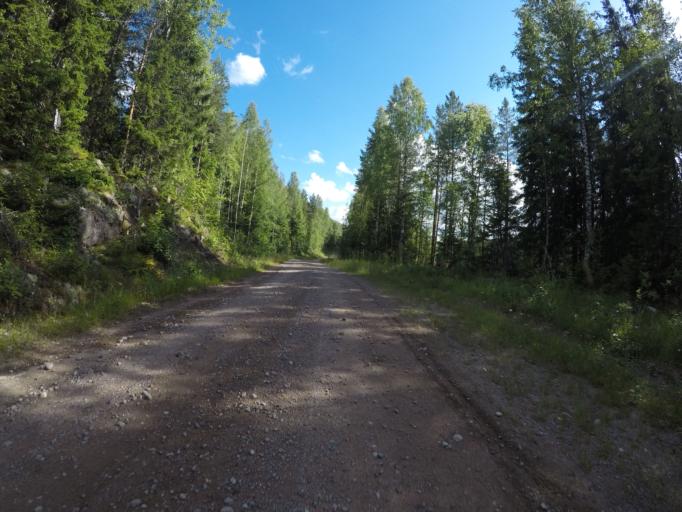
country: SE
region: OErebro
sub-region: Hallefors Kommun
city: Haellefors
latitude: 59.9966
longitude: 14.6054
